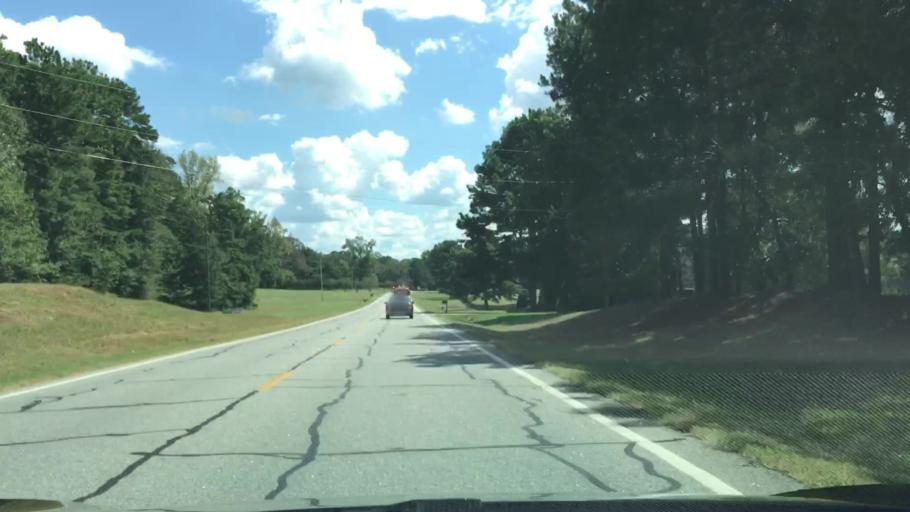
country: US
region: Georgia
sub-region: Oconee County
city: Watkinsville
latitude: 33.7547
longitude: -83.3043
